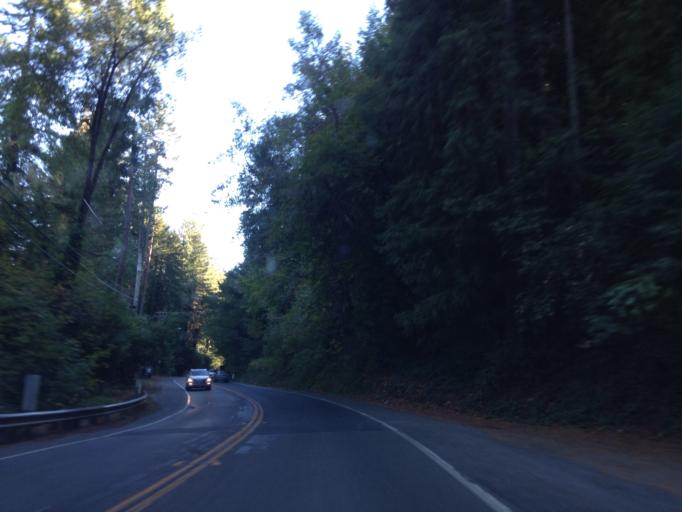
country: US
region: California
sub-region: Sonoma County
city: Monte Rio
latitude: 38.4878
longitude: -123.0160
